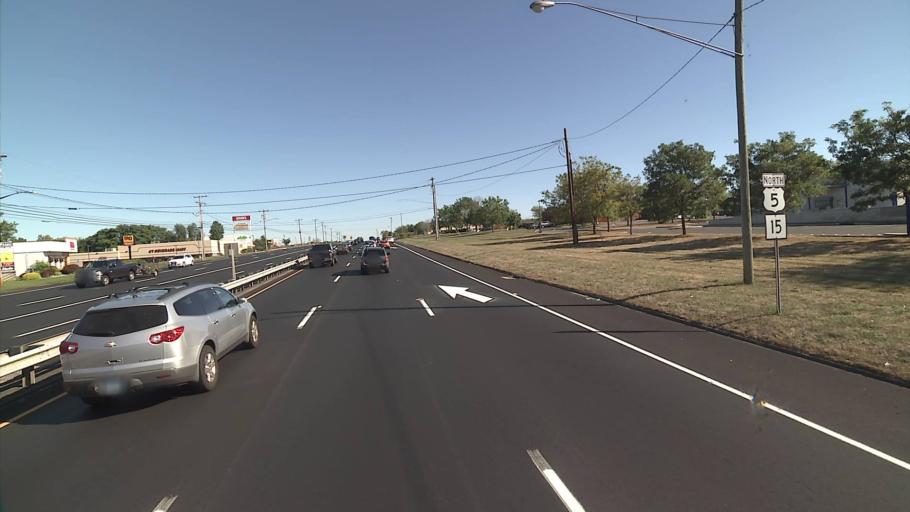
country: US
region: Connecticut
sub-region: Hartford County
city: Newington
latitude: 41.6621
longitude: -72.7219
